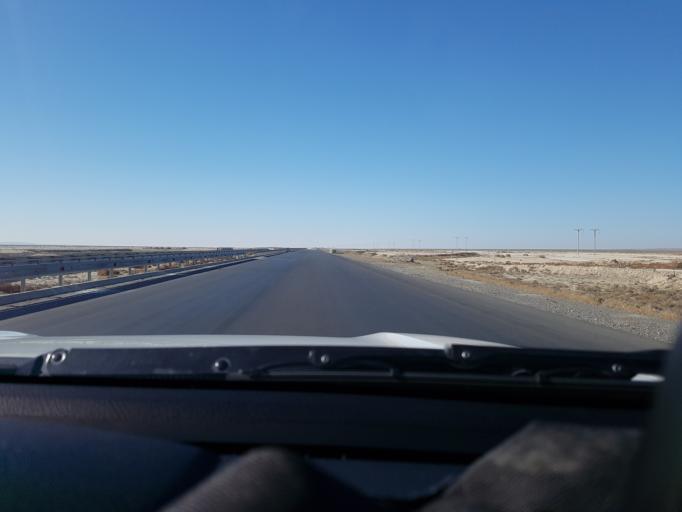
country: TM
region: Balkan
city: Gazanjyk
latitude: 39.2613
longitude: 55.1141
